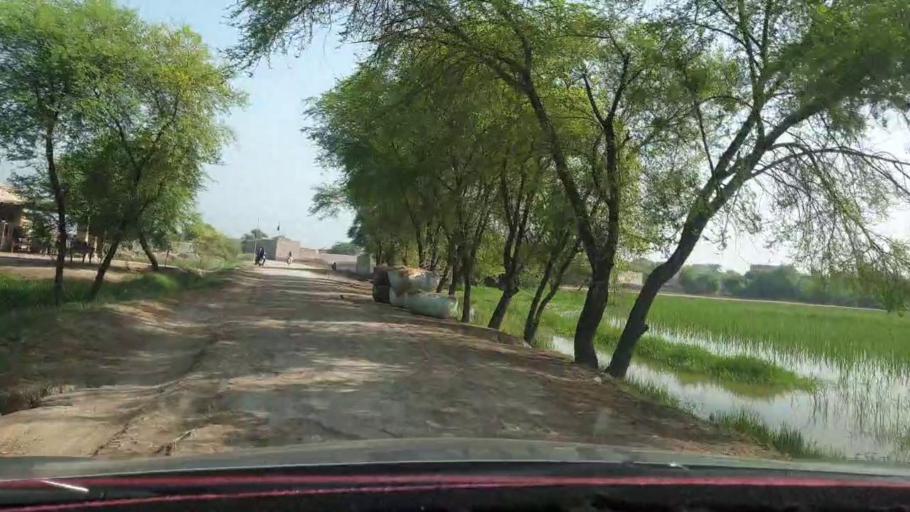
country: PK
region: Sindh
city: Nasirabad
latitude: 27.4600
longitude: 67.9186
